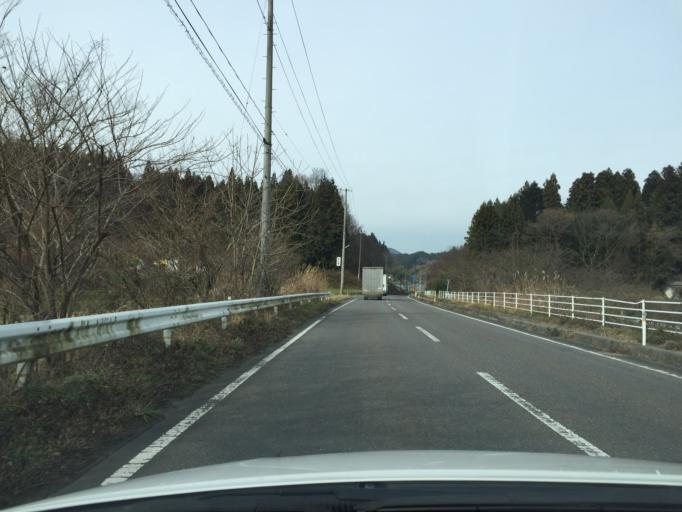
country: JP
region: Fukushima
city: Funehikimachi-funehiki
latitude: 37.2766
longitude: 140.6257
